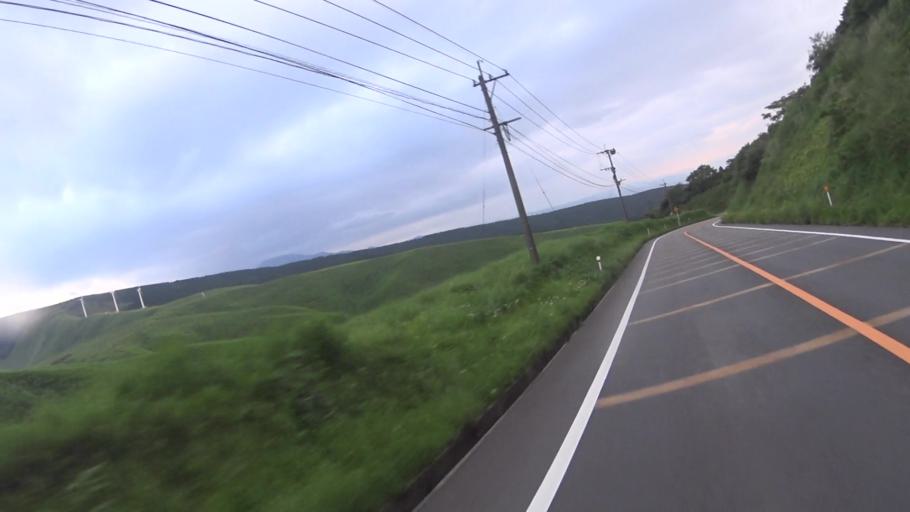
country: JP
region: Kumamoto
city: Ozu
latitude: 32.9157
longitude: 130.9646
